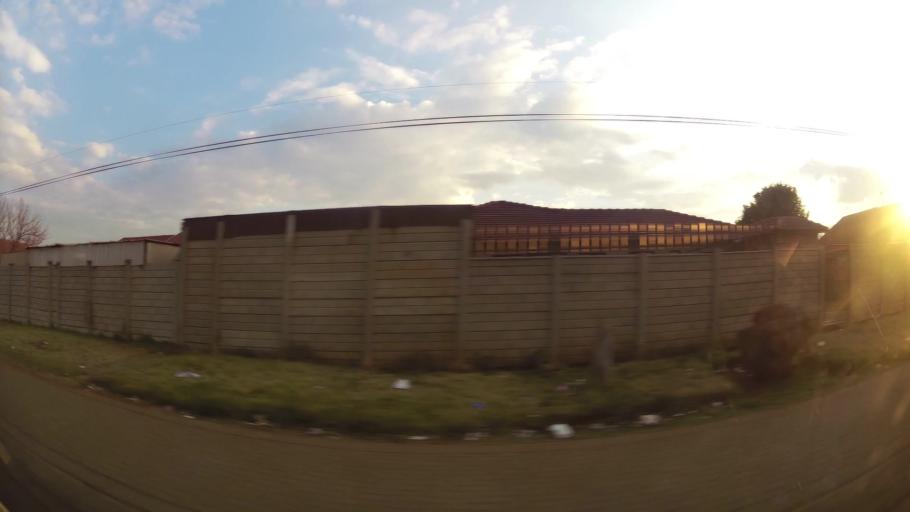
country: ZA
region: Gauteng
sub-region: City of Johannesburg Metropolitan Municipality
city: Orange Farm
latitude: -26.5646
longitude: 27.8622
